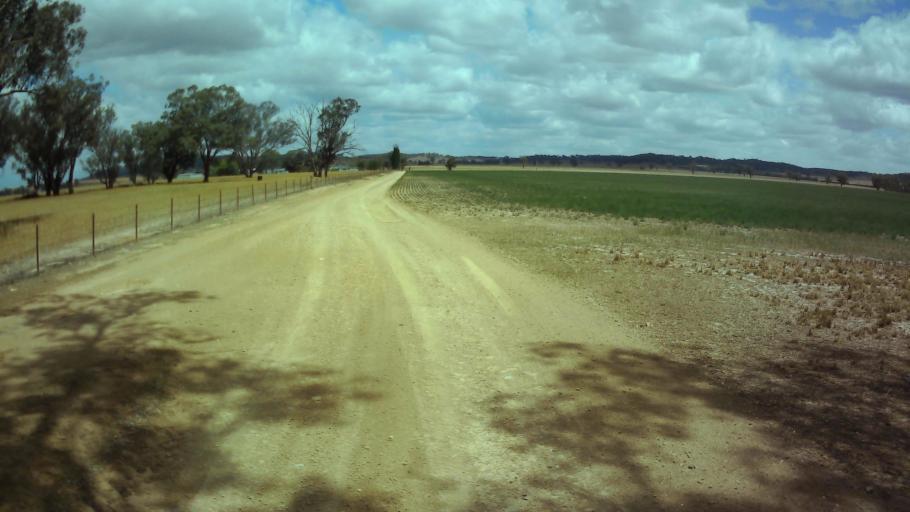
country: AU
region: New South Wales
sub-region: Weddin
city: Grenfell
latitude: -33.9796
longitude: 148.2642
